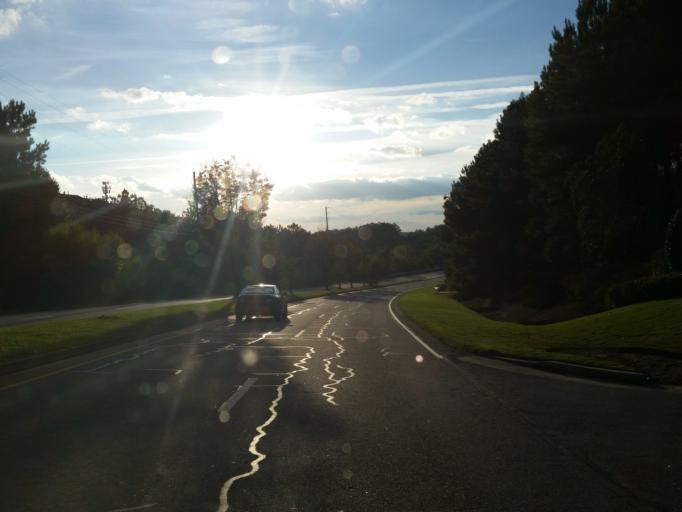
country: US
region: Georgia
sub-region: Cobb County
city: Smyrna
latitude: 33.8383
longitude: -84.5113
